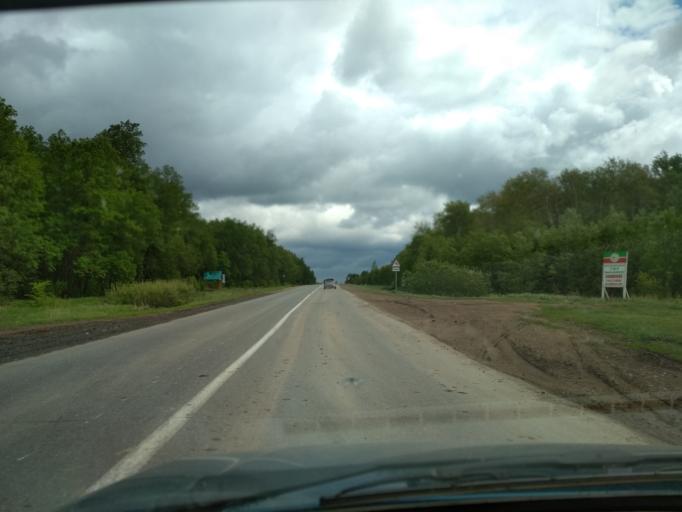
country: RU
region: Tatarstan
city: Zainsk
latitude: 55.3341
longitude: 51.9613
